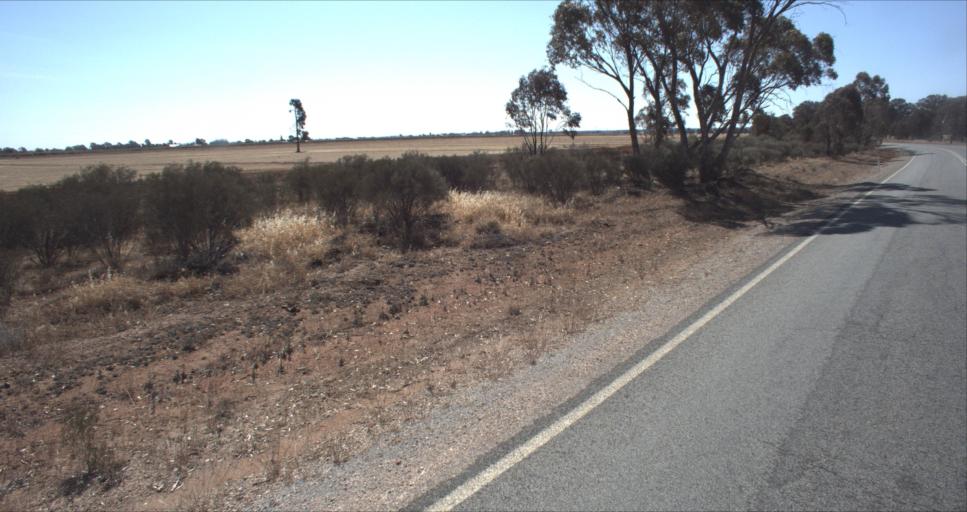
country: AU
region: New South Wales
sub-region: Leeton
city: Leeton
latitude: -34.4979
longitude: 146.4335
